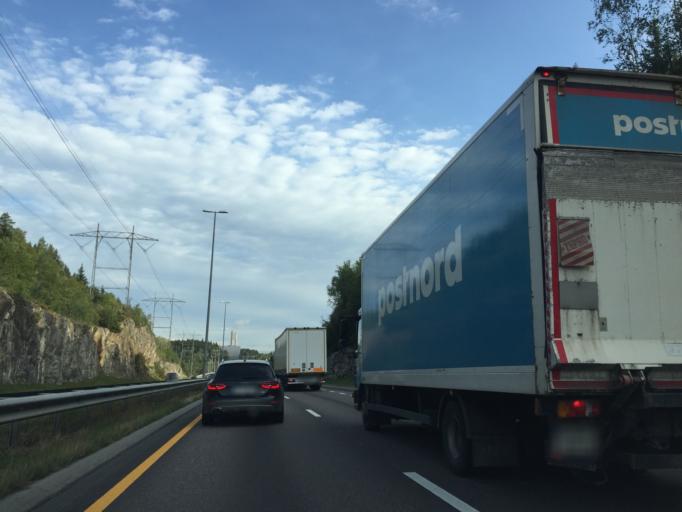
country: NO
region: Akershus
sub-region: Oppegard
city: Kolbotn
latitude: 59.8285
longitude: 10.8433
